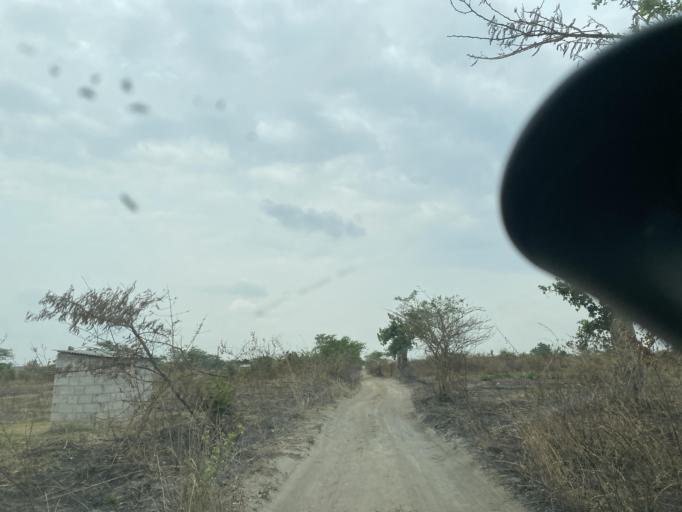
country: ZM
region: Lusaka
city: Lusaka
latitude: -15.2361
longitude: 28.3344
